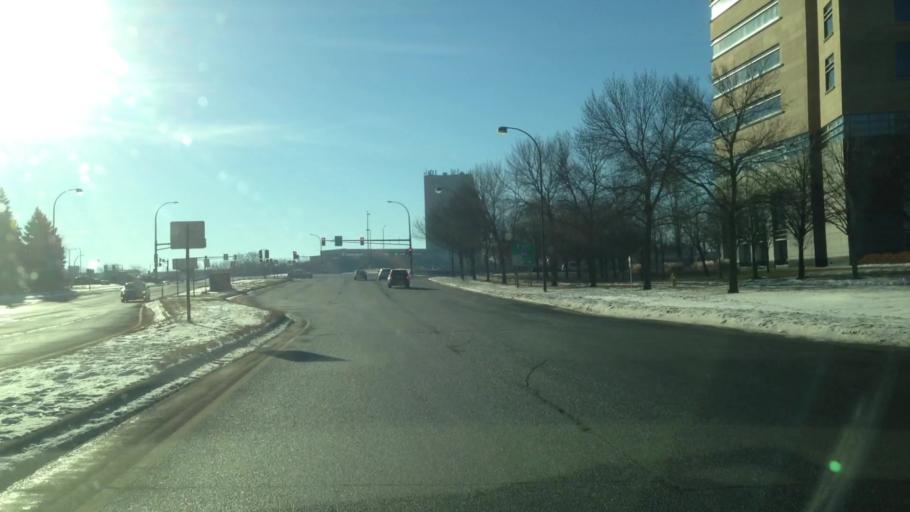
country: US
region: Minnesota
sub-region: Hennepin County
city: Saint Louis Park
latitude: 44.9722
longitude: -93.3520
